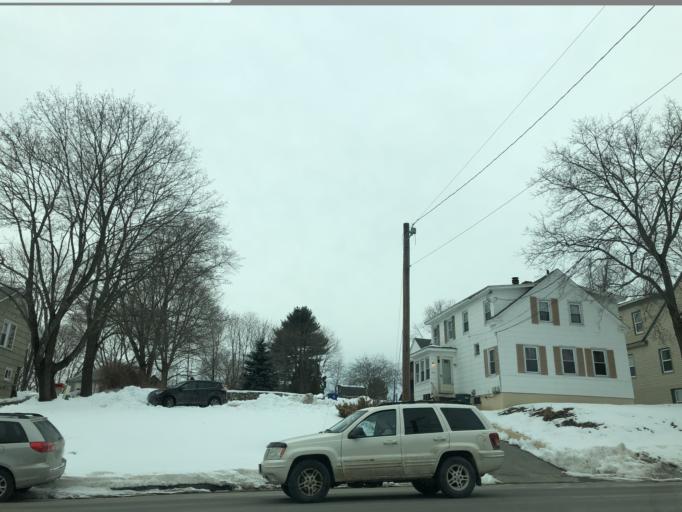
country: US
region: Maine
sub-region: Cumberland County
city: Westbrook
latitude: 43.6812
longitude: -70.3676
